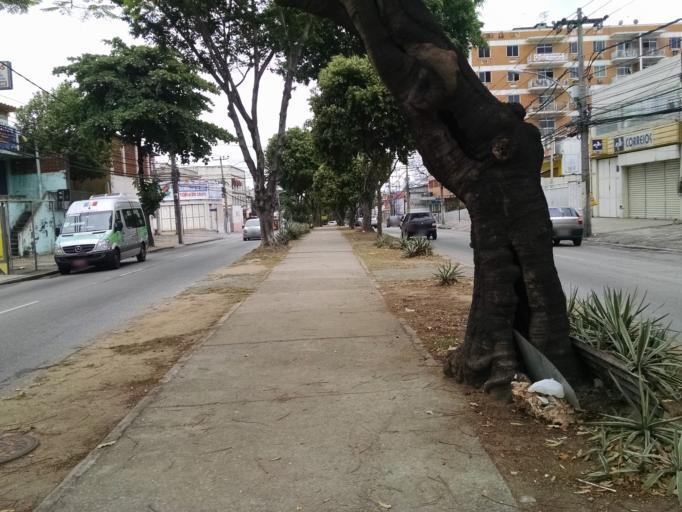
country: BR
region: Rio de Janeiro
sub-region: Duque De Caxias
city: Duque de Caxias
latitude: -22.8288
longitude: -43.3101
